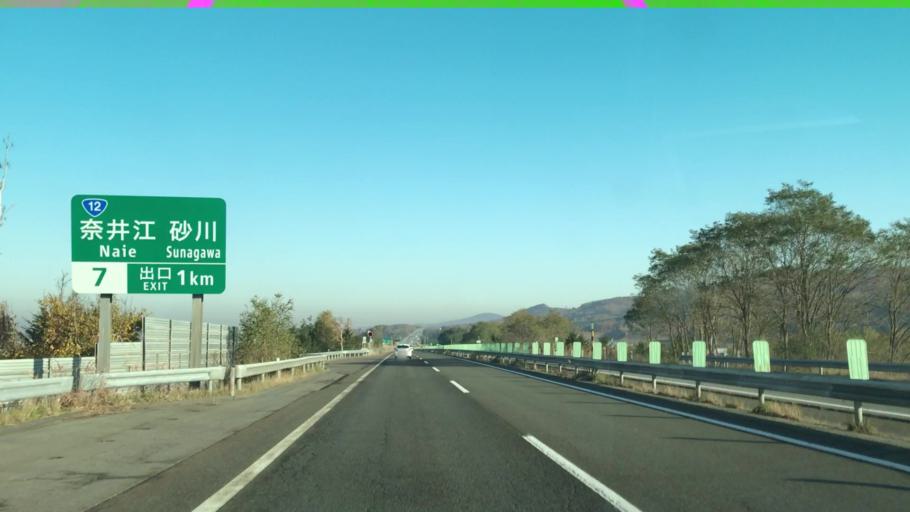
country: JP
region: Hokkaido
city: Sunagawa
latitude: 43.4395
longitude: 141.9161
